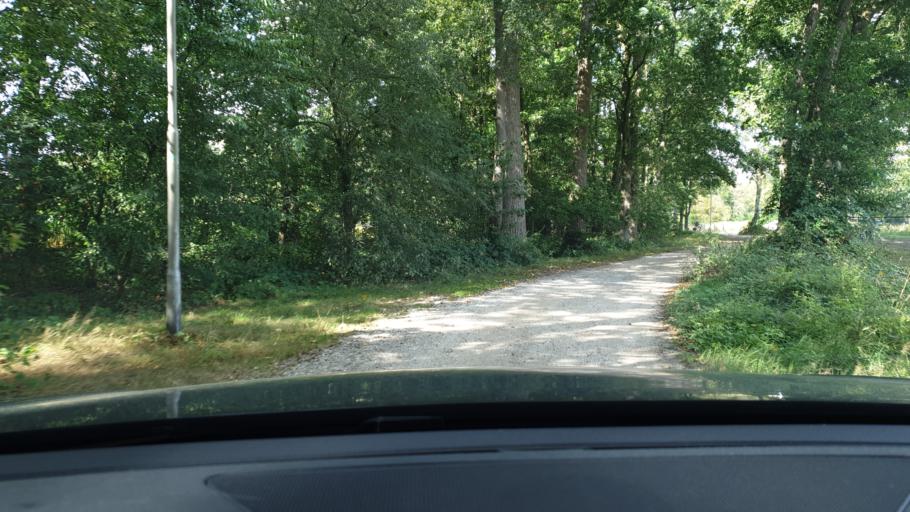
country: NL
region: North Brabant
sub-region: Gemeente Valkenswaard
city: Valkenswaard
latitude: 51.3432
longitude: 5.4838
